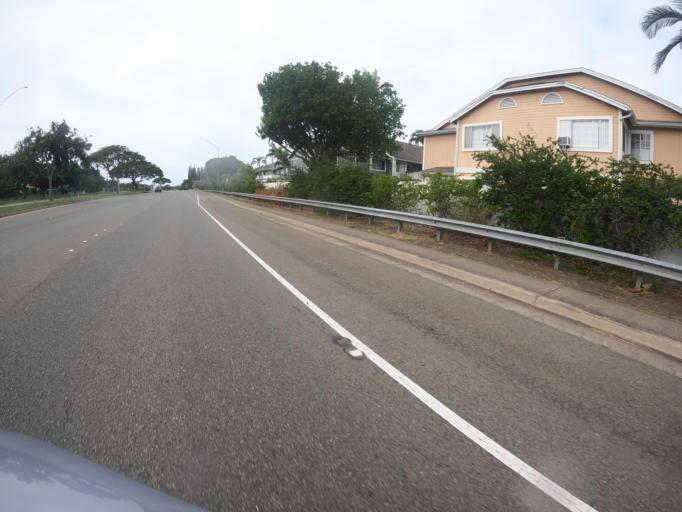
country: US
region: Hawaii
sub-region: Honolulu County
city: Halawa
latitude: 21.3687
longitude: -157.9223
